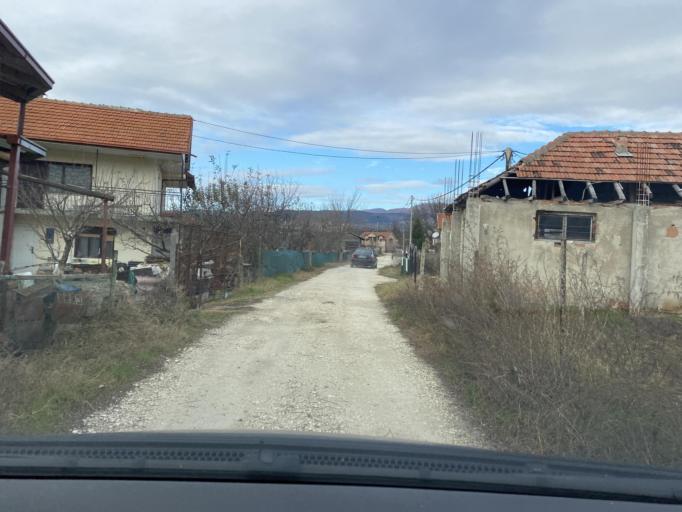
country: MK
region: Opstina Rankovce
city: Rankovce
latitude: 42.1686
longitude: 22.1572
